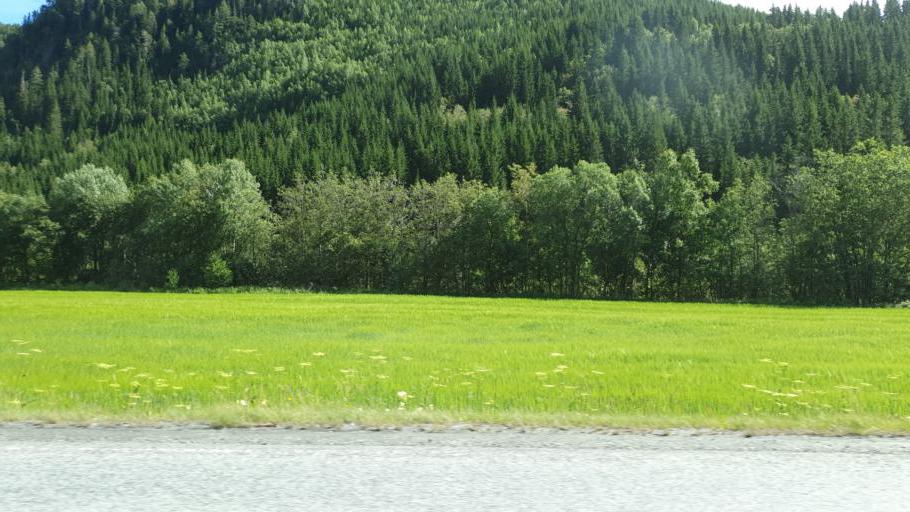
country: NO
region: Sor-Trondelag
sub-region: Midtre Gauldal
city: Storen
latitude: 62.9988
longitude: 10.2388
